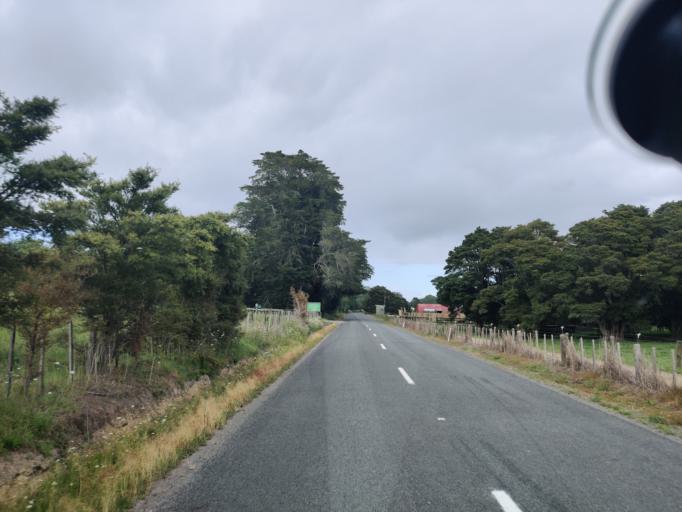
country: NZ
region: Northland
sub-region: Whangarei
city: Ngunguru
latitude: -35.5629
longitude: 174.3829
